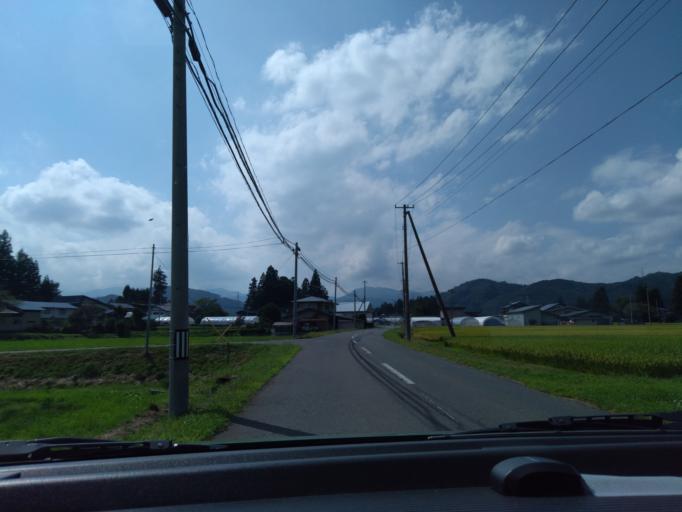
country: JP
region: Iwate
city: Shizukuishi
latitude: 39.6857
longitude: 140.9396
